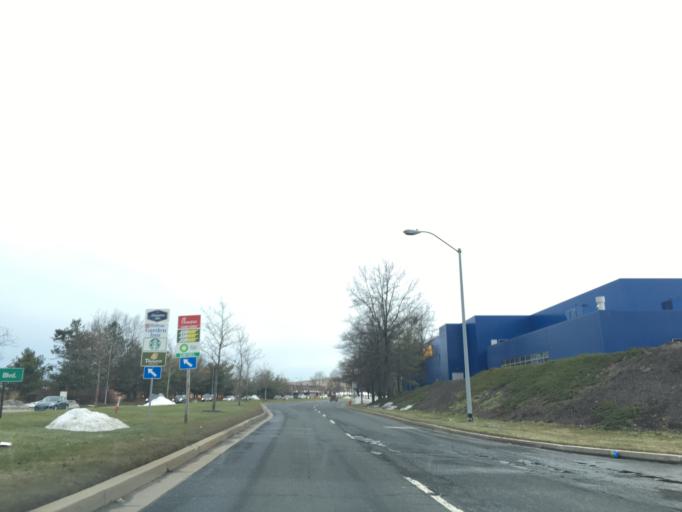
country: US
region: Maryland
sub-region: Baltimore County
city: White Marsh
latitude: 39.3759
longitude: -76.4606
